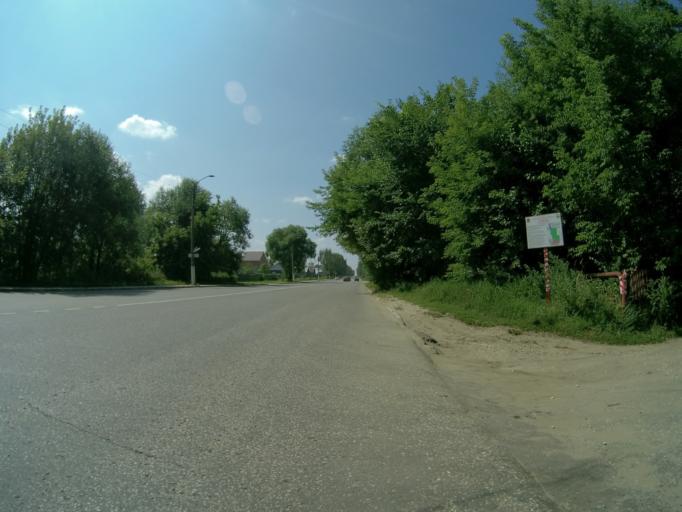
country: RU
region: Vladimir
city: Gus'-Khrustal'nyy
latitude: 55.6280
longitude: 40.6878
